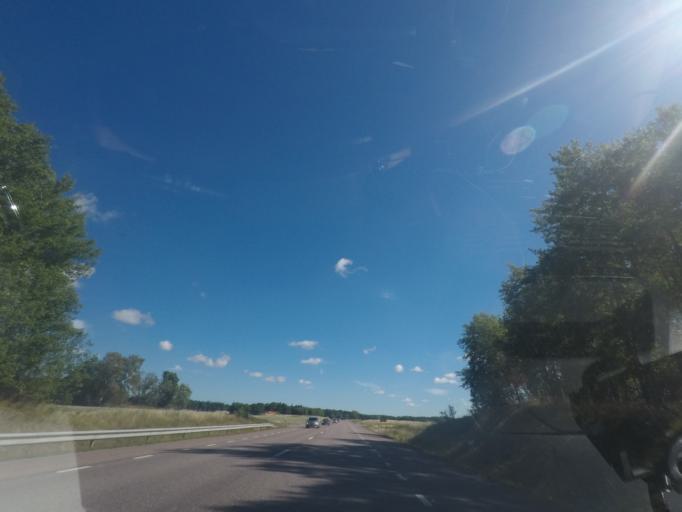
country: SE
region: Uppsala
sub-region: Uppsala Kommun
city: Uppsala
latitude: 59.8140
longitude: 17.4795
